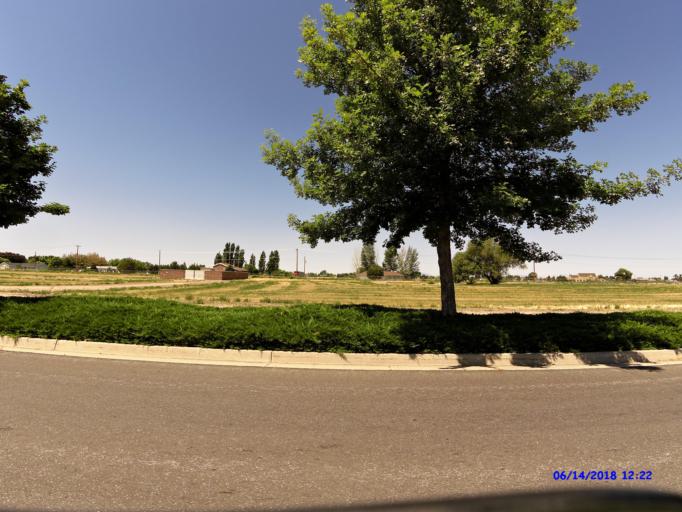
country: US
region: Utah
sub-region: Weber County
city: Marriott-Slaterville
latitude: 41.2631
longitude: -112.0074
